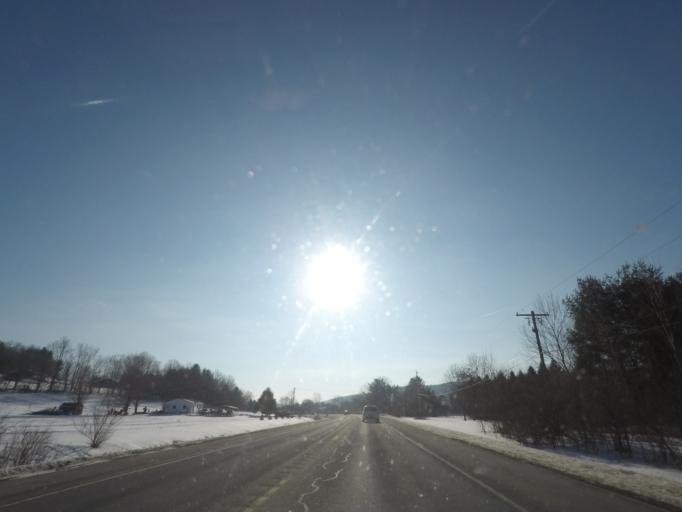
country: US
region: Massachusetts
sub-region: Berkshire County
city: Pittsfield
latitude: 42.5157
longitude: -73.3629
